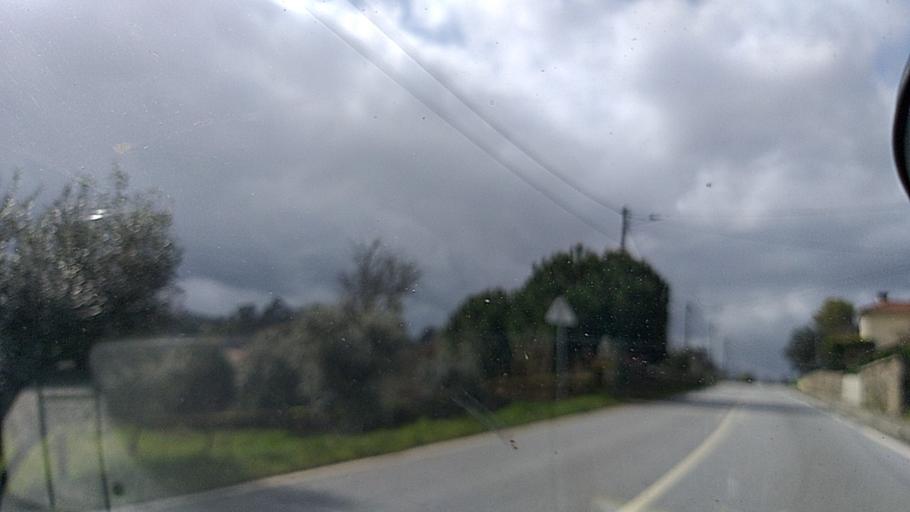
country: PT
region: Viseu
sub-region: Mangualde
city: Mangualde
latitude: 40.6221
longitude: -7.7553
